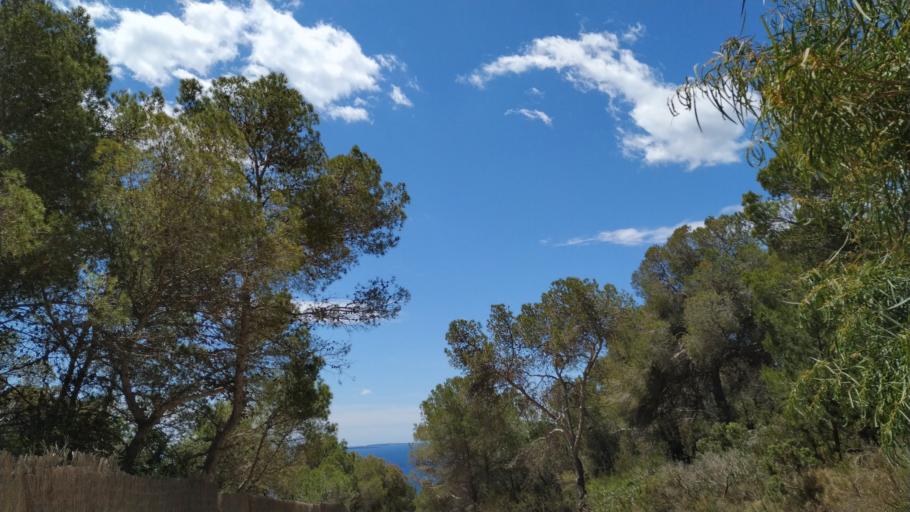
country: ES
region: Balearic Islands
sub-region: Illes Balears
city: Ibiza
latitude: 38.9220
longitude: 1.4749
